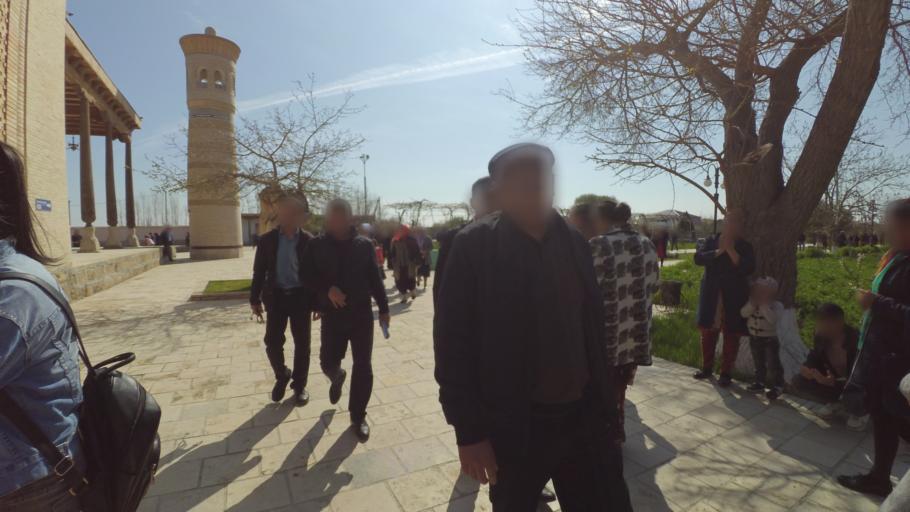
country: UZ
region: Bukhara
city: Kogon
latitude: 39.8053
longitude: 64.5400
